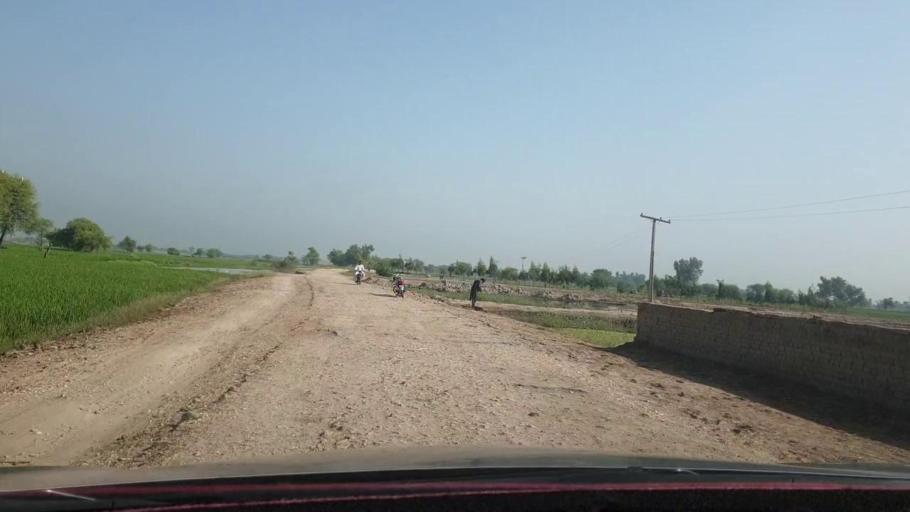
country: PK
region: Sindh
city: Nasirabad
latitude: 27.4547
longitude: 67.9176
